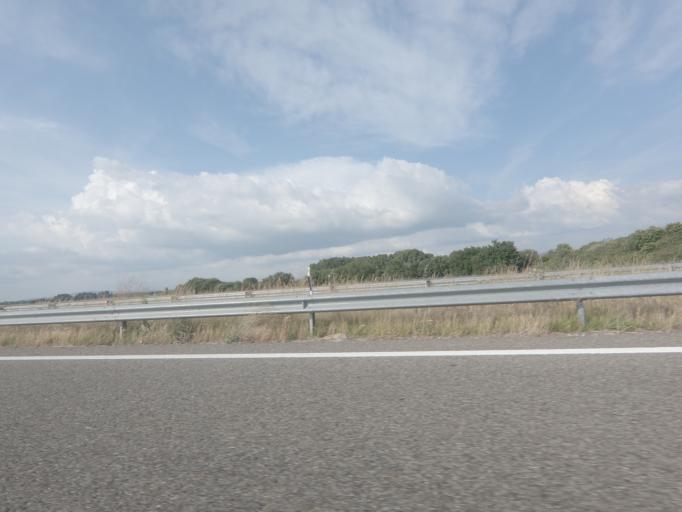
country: ES
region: Galicia
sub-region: Provincia de Ourense
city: Xinzo de Limia
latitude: 42.0856
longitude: -7.7186
